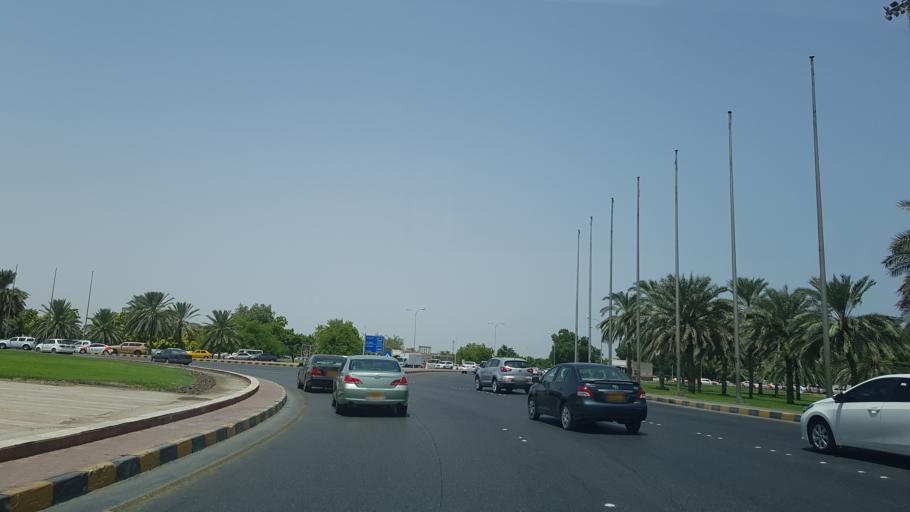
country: OM
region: Muhafazat Masqat
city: As Sib al Jadidah
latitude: 23.5874
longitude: 58.2526
